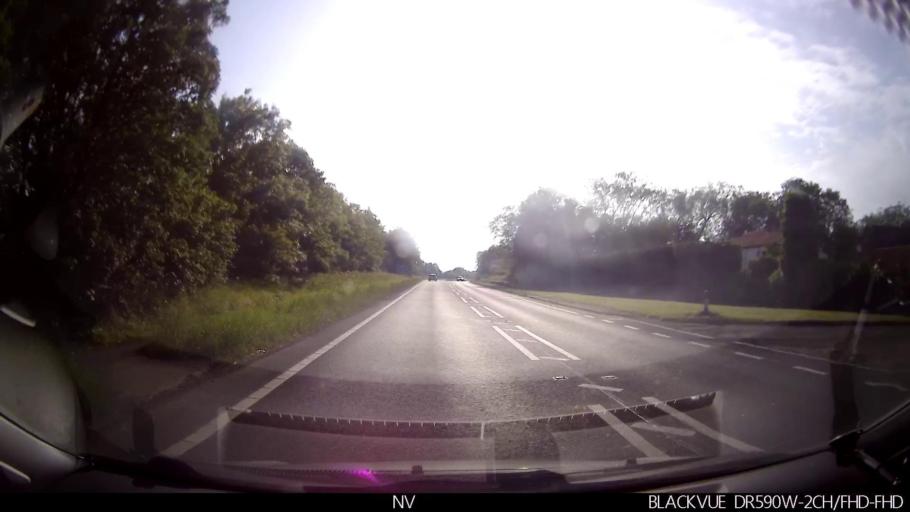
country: GB
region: England
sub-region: North Yorkshire
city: Thorpe Bassett
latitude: 54.1421
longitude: -0.7364
